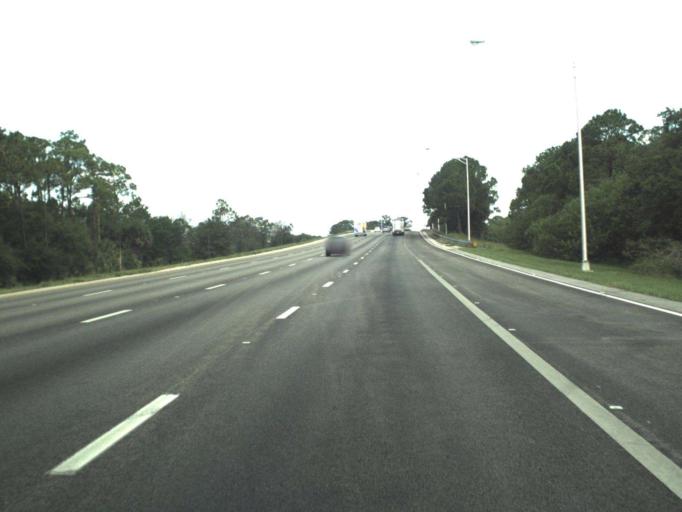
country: US
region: Florida
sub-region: Saint Lucie County
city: Lakewood Park
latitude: 27.4676
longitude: -80.4221
